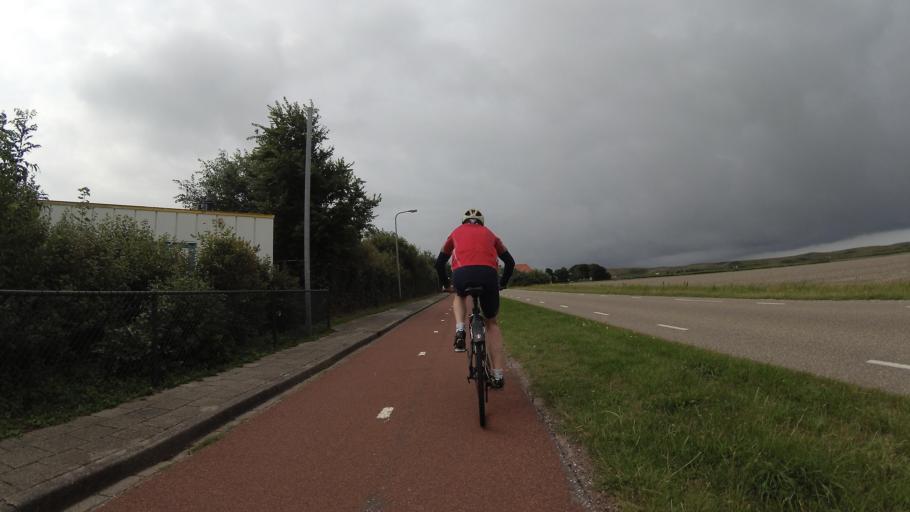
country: NL
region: North Holland
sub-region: Gemeente Schagen
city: Schagen
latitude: 52.8469
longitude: 4.7144
